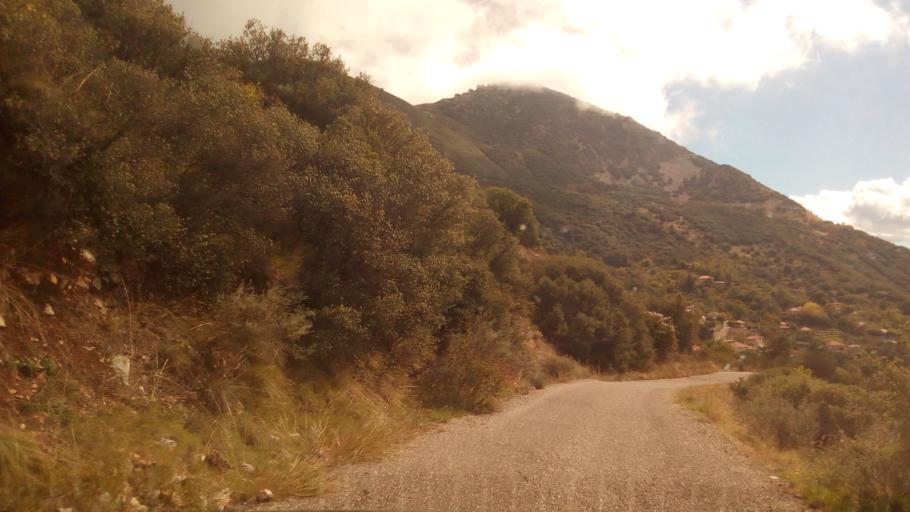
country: GR
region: West Greece
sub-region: Nomos Aitolias kai Akarnanias
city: Nafpaktos
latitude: 38.4957
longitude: 21.8475
